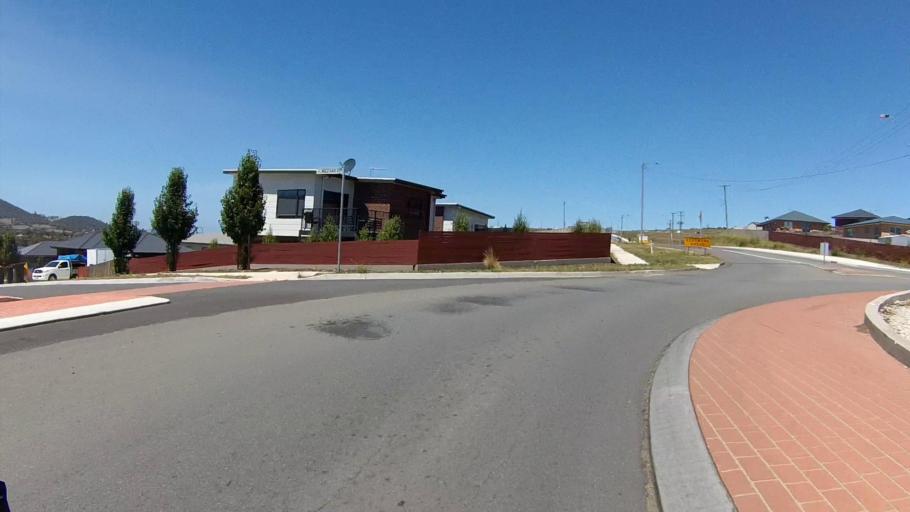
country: AU
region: Tasmania
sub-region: Clarence
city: Howrah
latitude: -42.8839
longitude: 147.4285
